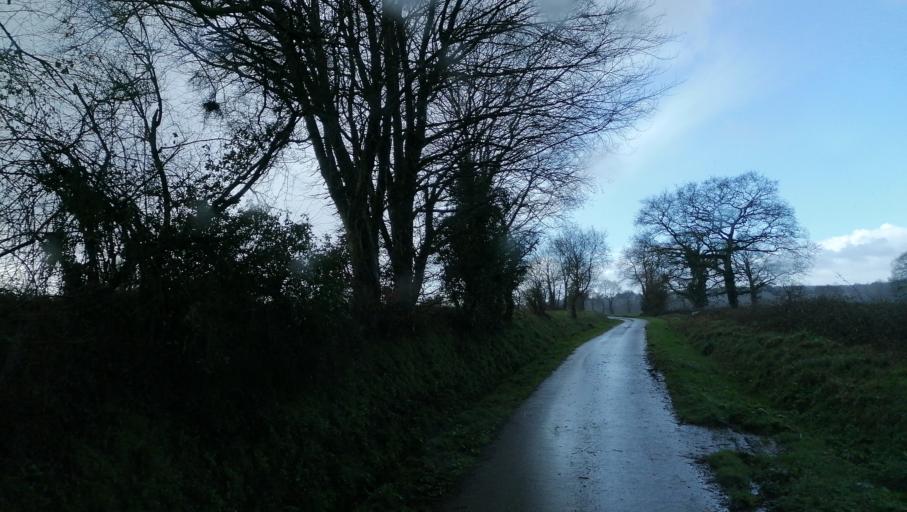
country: FR
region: Brittany
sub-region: Departement des Cotes-d'Armor
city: Lanrodec
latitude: 48.4927
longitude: -3.0310
